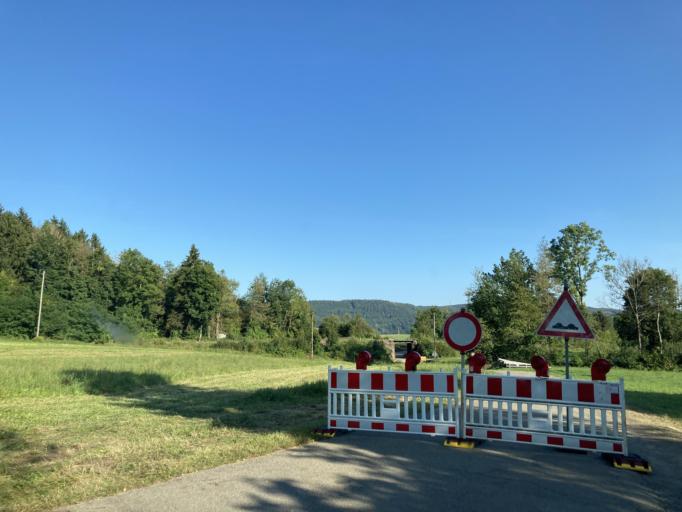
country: DE
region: Baden-Wuerttemberg
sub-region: Freiburg Region
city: Blumberg
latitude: 47.8158
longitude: 8.5149
